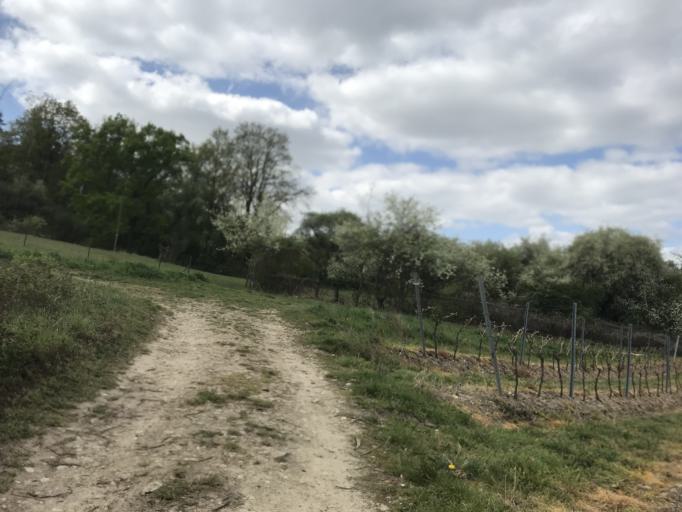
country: DE
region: Rheinland-Pfalz
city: Wackernheim
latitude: 49.9867
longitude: 8.1071
